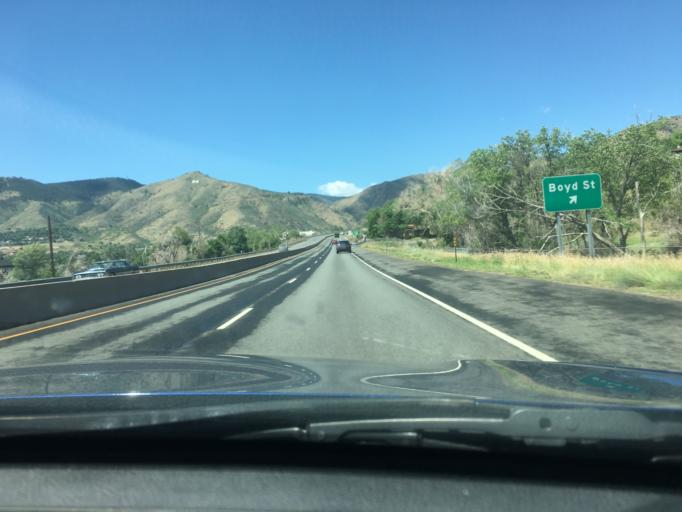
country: US
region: Colorado
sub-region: Jefferson County
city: Golden
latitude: 39.7638
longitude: -105.2157
